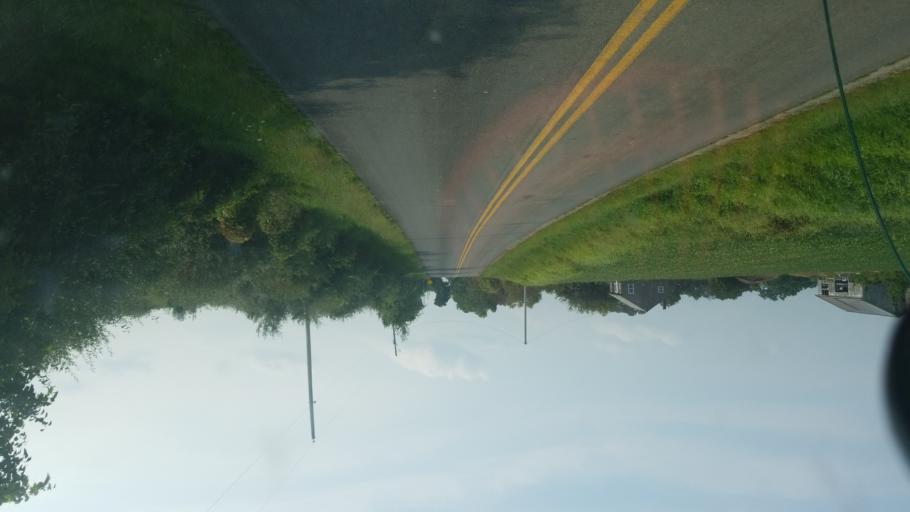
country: US
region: Ohio
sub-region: Medina County
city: Medina
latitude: 41.0965
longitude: -81.8841
